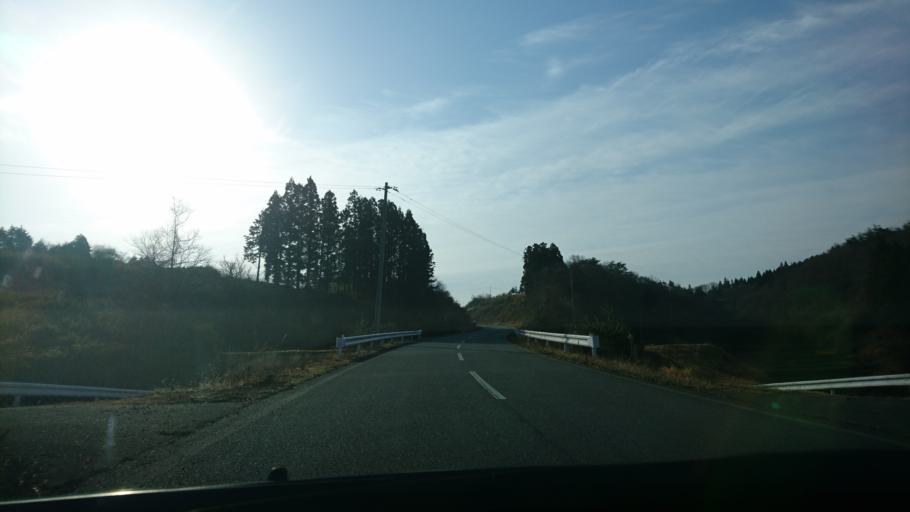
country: JP
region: Iwate
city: Ichinoseki
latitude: 38.8657
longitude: 141.1919
